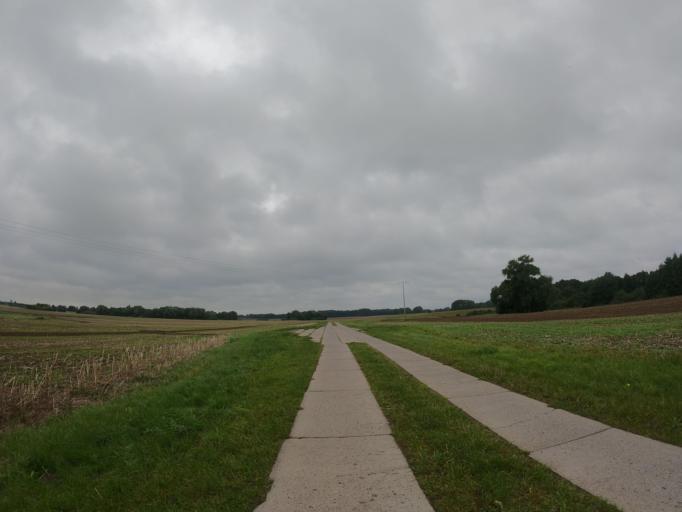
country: DE
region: Mecklenburg-Vorpommern
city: Poseritz
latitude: 54.2783
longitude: 13.2433
